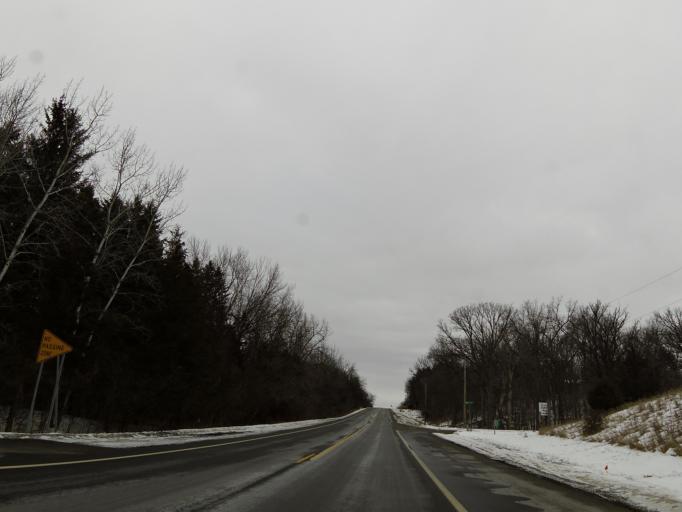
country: US
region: Wisconsin
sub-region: Pierce County
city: Prescott
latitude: 44.7996
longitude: -92.8064
